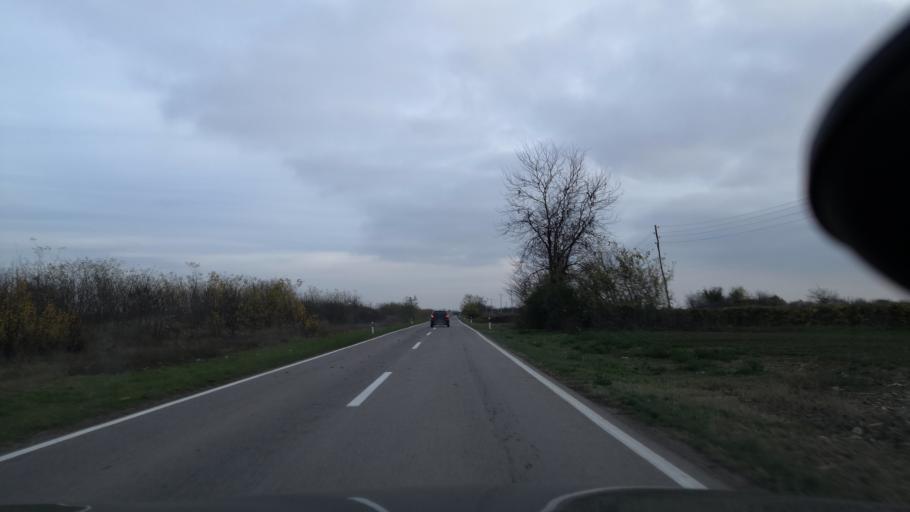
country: RS
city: Sanad
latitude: 45.9725
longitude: 20.1210
